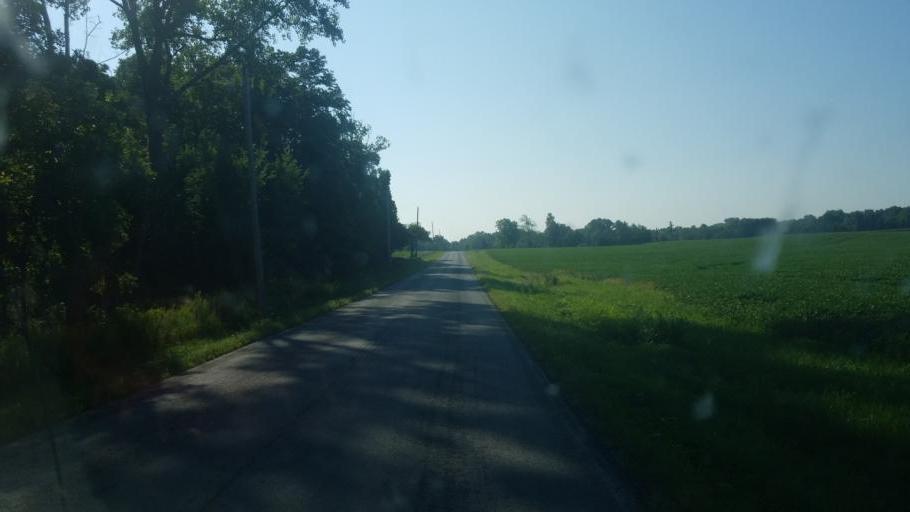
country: US
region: Ohio
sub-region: Huron County
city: New London
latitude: 41.0789
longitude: -82.3396
